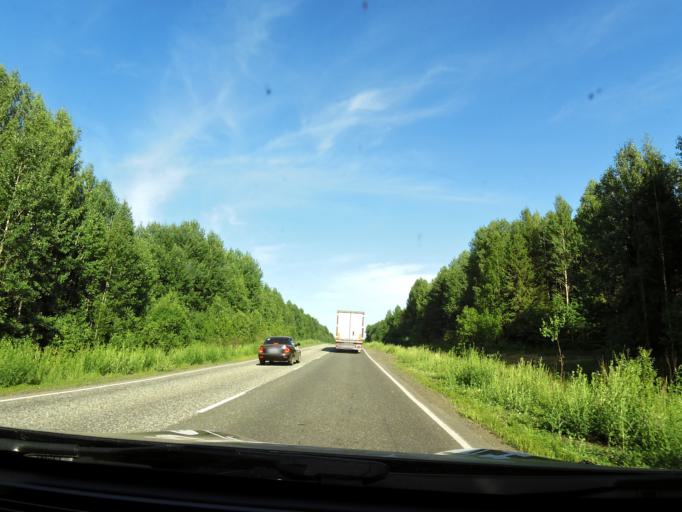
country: RU
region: Kirov
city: Chernaya Kholunitsa
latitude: 58.8823
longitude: 51.4243
